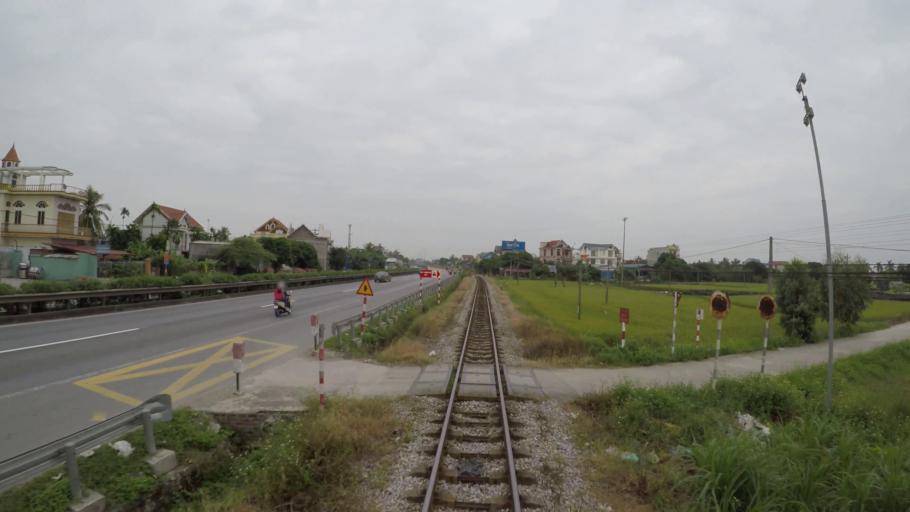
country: VN
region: Hai Duong
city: Phu Thai
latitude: 20.9551
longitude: 106.5283
